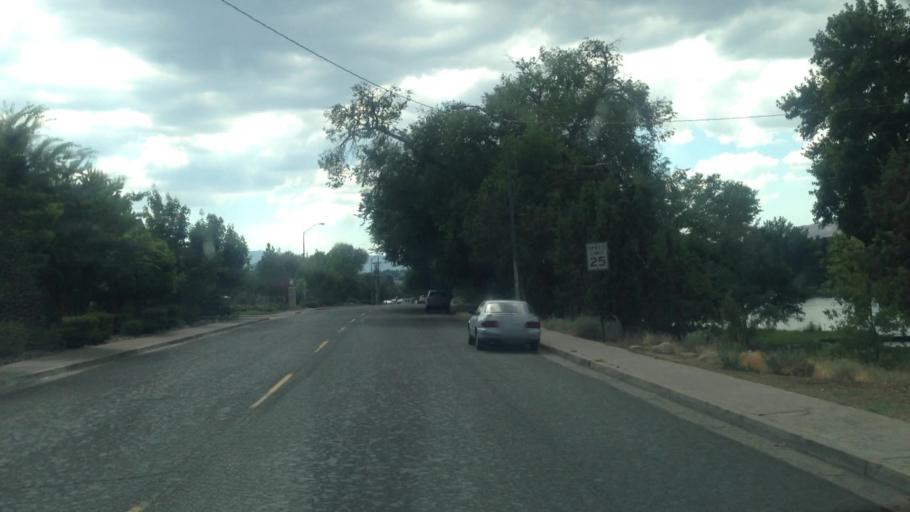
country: US
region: Nevada
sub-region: Washoe County
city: Reno
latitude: 39.5199
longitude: -119.8285
